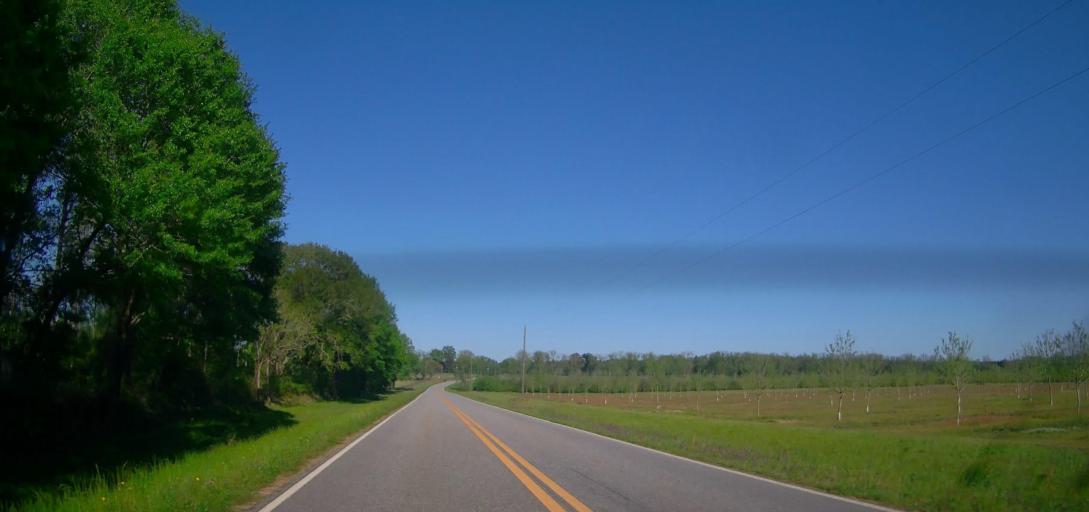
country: US
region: Georgia
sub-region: Houston County
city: Perry
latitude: 32.4517
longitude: -83.6451
